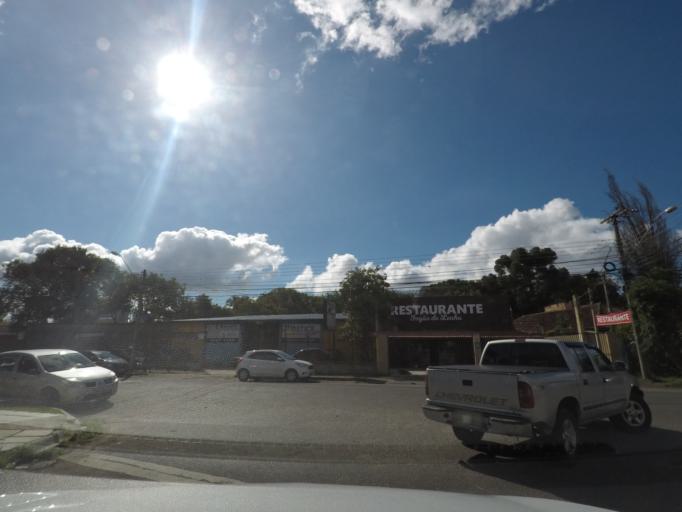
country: BR
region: Parana
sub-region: Curitiba
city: Curitiba
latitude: -25.4555
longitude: -49.2537
